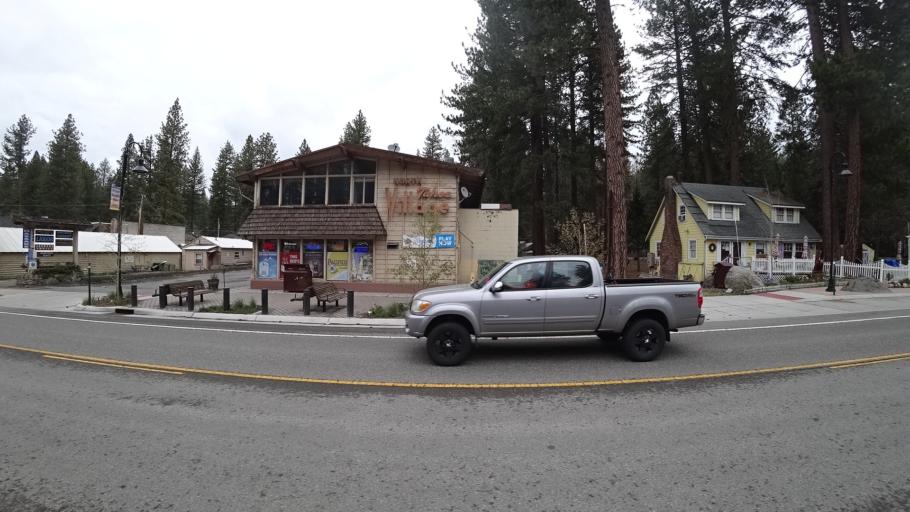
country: US
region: California
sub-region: Placer County
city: Kings Beach
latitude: 39.2355
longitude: -120.0209
